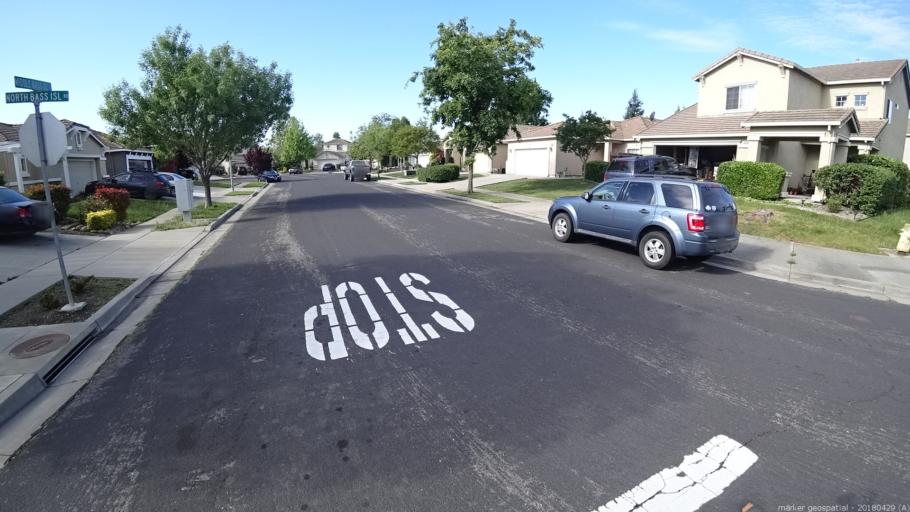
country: US
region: California
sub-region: Yolo County
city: West Sacramento
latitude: 38.5410
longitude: -121.5654
